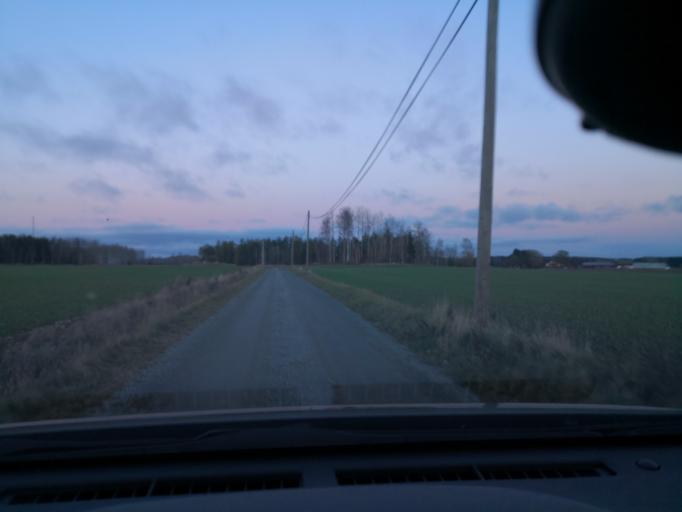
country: SE
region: Vaestmanland
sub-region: Vasteras
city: Tillberga
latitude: 59.7902
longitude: 16.6288
